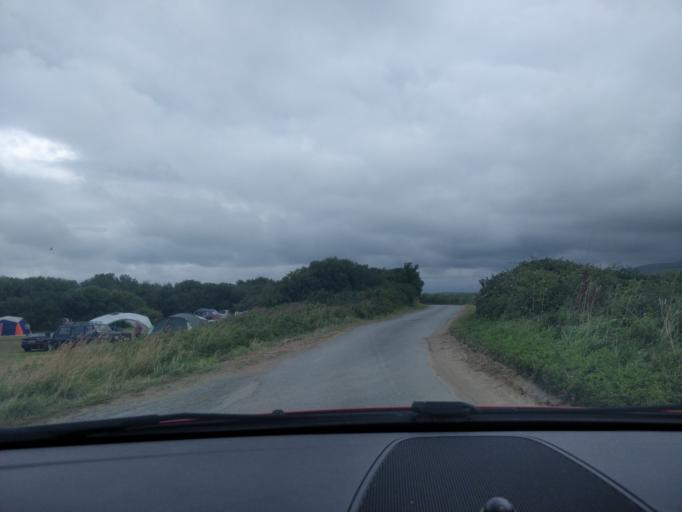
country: GB
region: Wales
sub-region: Gwynedd
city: Llanfair
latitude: 52.8121
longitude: -4.1421
